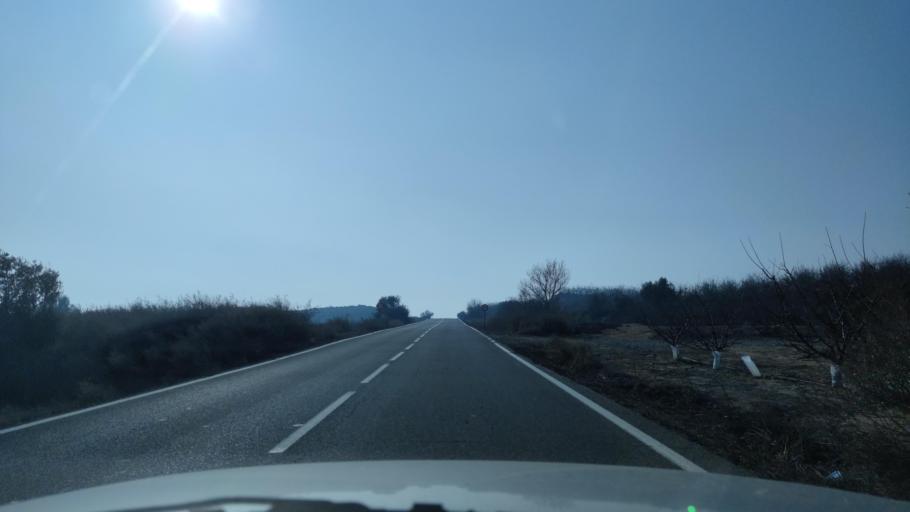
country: ES
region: Catalonia
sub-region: Provincia de Lleida
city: Seros
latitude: 41.4716
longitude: 0.3810
